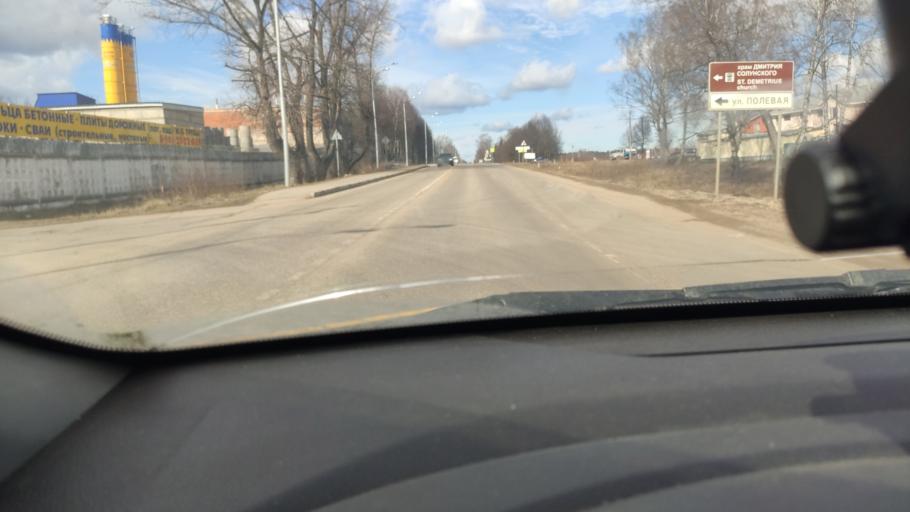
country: RU
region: Moskovskaya
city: Ruza
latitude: 55.7100
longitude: 36.1802
